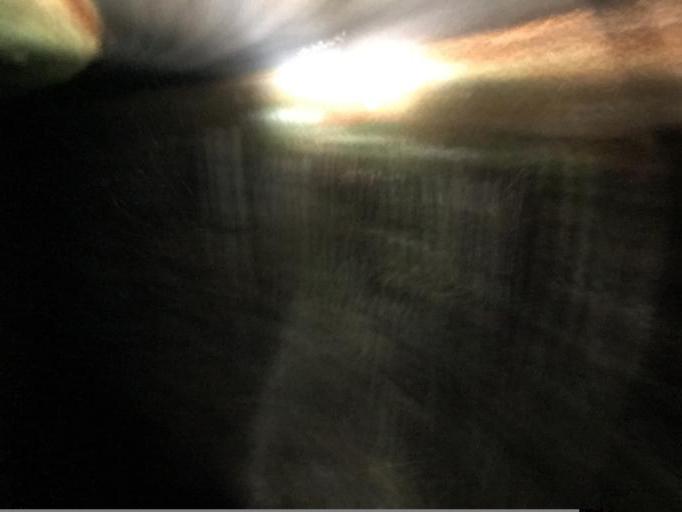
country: FR
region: Auvergne
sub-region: Departement du Puy-de-Dome
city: Saint-Remy-sur-Durolle
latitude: 45.9439
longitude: 3.6435
